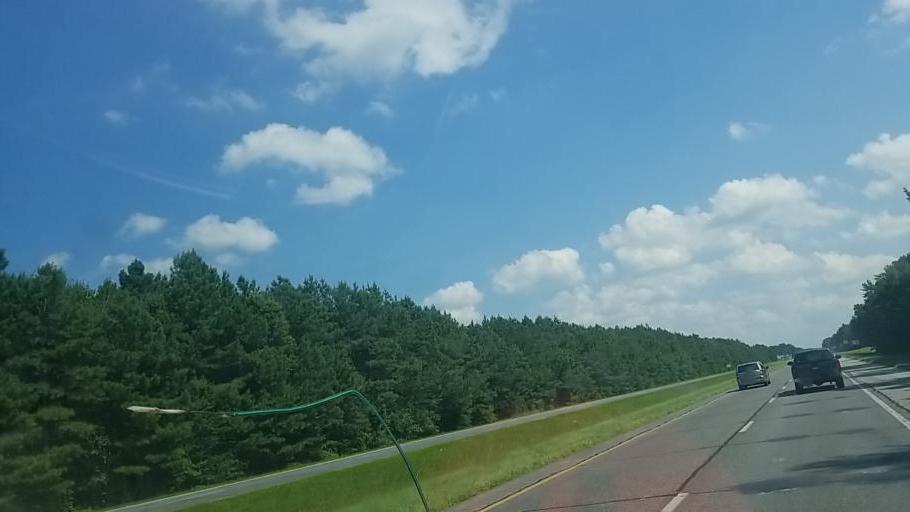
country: US
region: Delaware
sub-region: Sussex County
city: Georgetown
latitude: 38.7456
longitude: -75.4294
